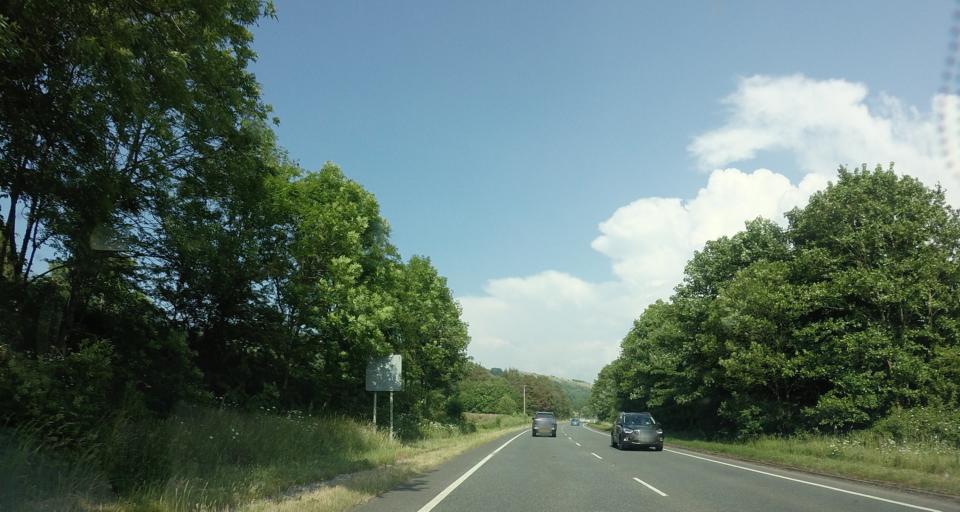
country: GB
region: England
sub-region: Cumbria
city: Cockermouth
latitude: 54.6588
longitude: -3.3204
